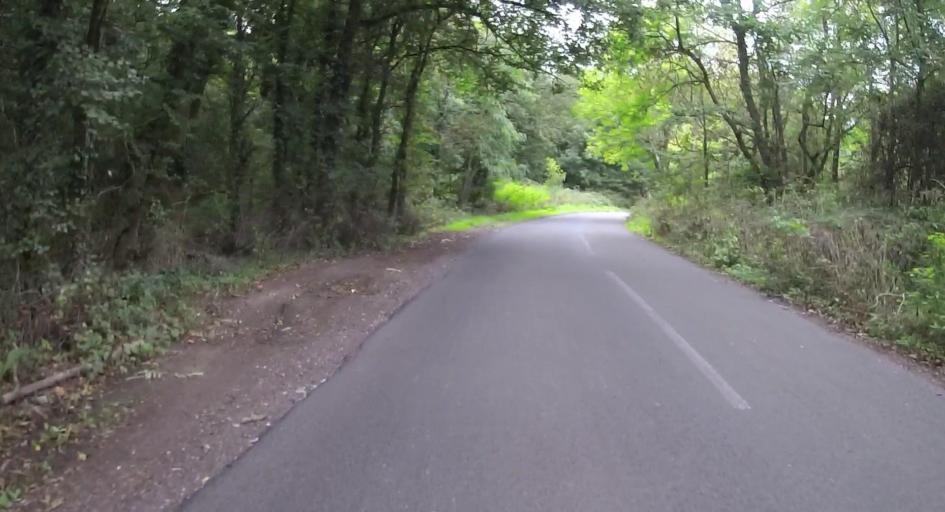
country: GB
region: England
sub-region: Surrey
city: Knaphill
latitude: 51.3271
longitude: -0.6239
